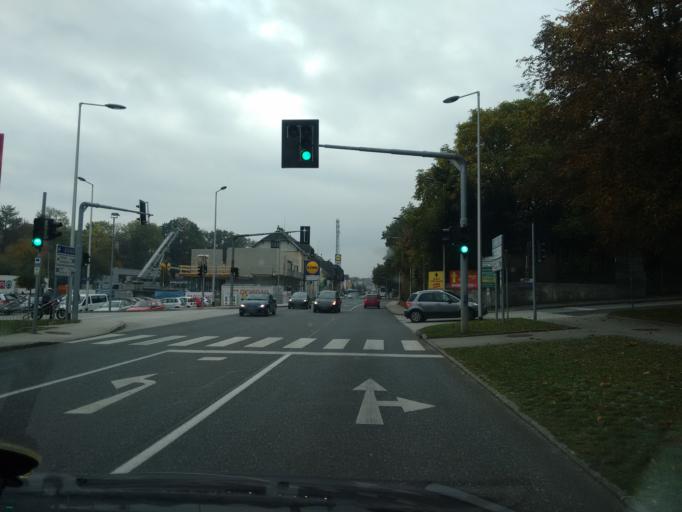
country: AT
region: Upper Austria
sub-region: Politischer Bezirk Steyr-Land
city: Bad Hall
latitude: 48.0383
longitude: 14.2085
